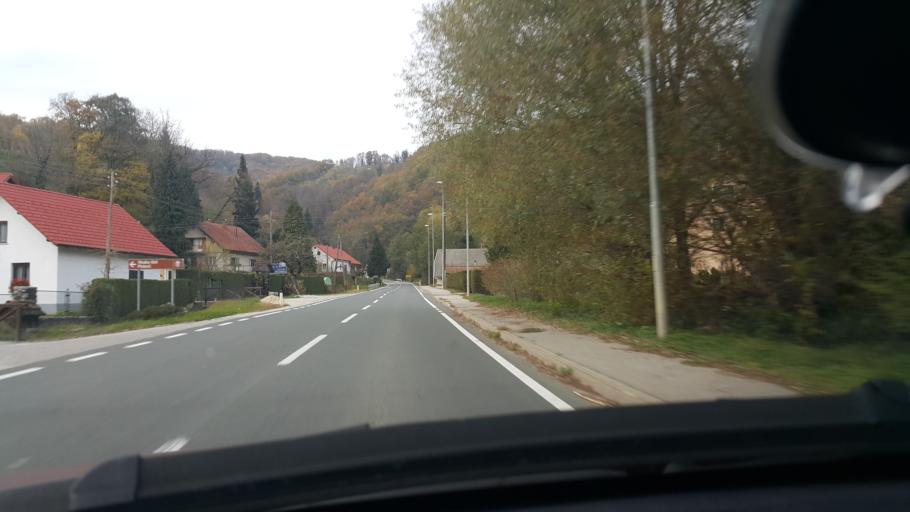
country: SI
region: Bistrica ob Sotli
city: Bistrica ob Sotli
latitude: 46.0223
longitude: 15.6901
